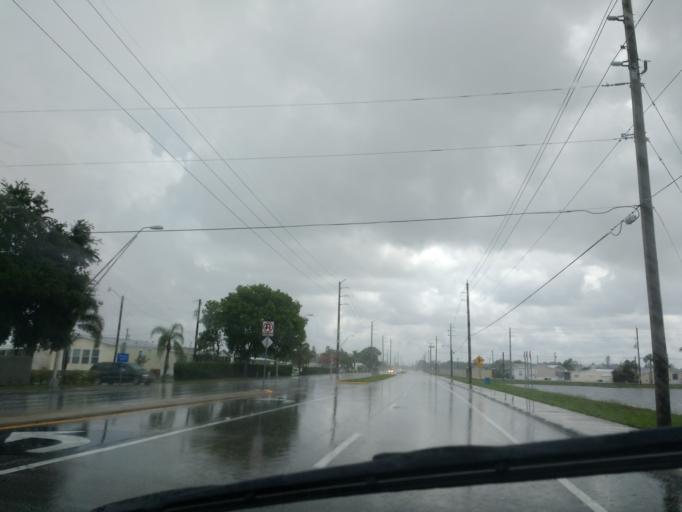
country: US
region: Florida
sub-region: Charlotte County
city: Charlotte Park
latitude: 26.8832
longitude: -82.0233
